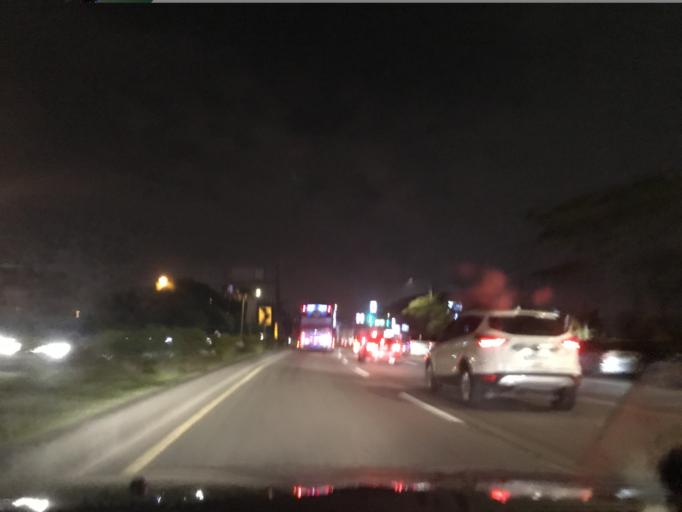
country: TW
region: Taiwan
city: Daxi
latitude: 24.8940
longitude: 121.2623
